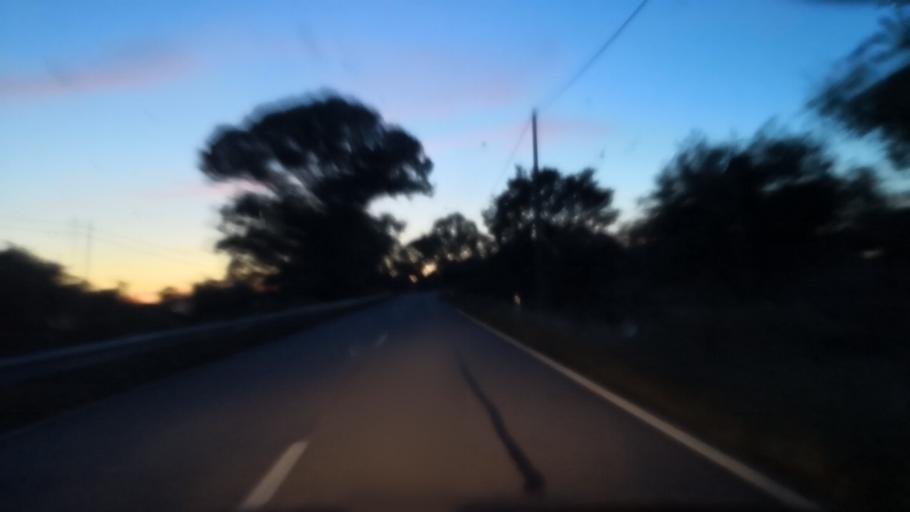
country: ES
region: Extremadura
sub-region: Provincia de Caceres
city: Piedras Albas
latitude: 39.8590
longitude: -7.0013
